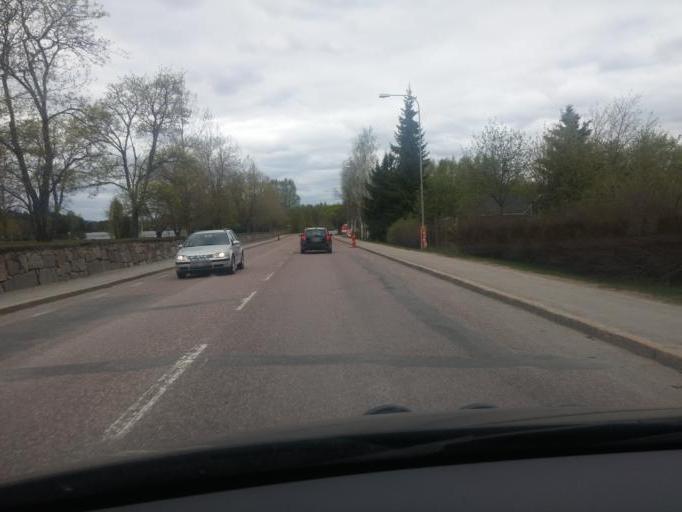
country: SE
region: Gaevleborg
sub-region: Ljusdals Kommun
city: Ljusdal
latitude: 61.8298
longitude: 16.0713
